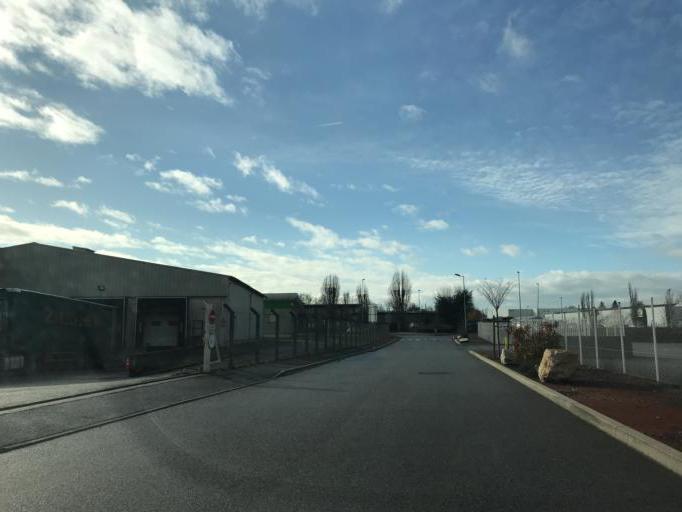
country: FR
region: Rhone-Alpes
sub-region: Departement de l'Ain
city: Reyrieux
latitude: 45.9455
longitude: 4.8155
